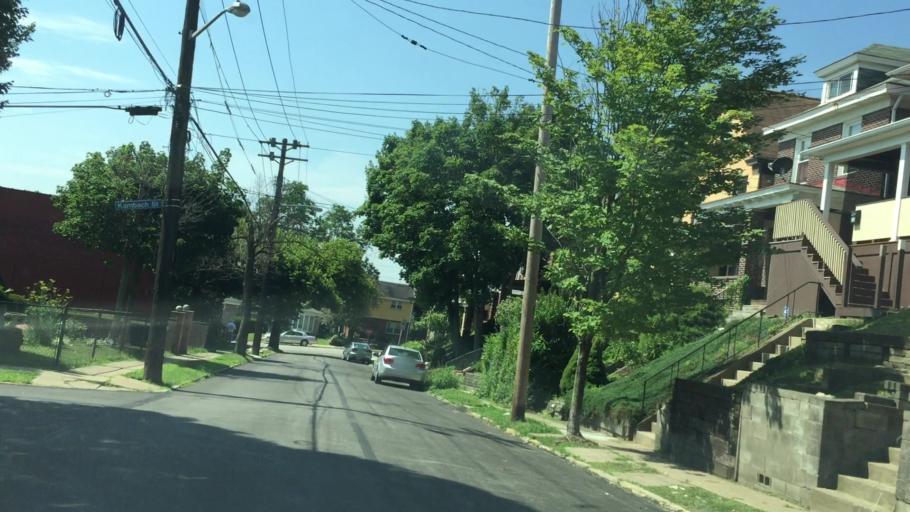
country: US
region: Pennsylvania
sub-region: Allegheny County
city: Pittsburgh
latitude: 40.4264
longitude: -80.0026
